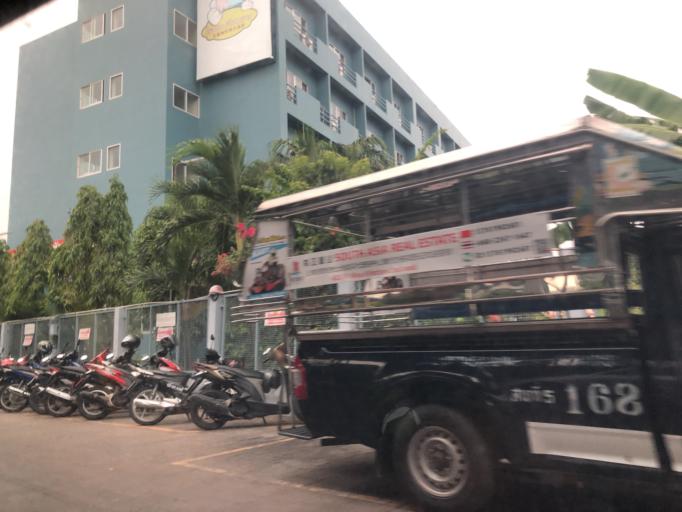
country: TH
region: Chon Buri
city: Phatthaya
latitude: 12.9493
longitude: 100.9034
